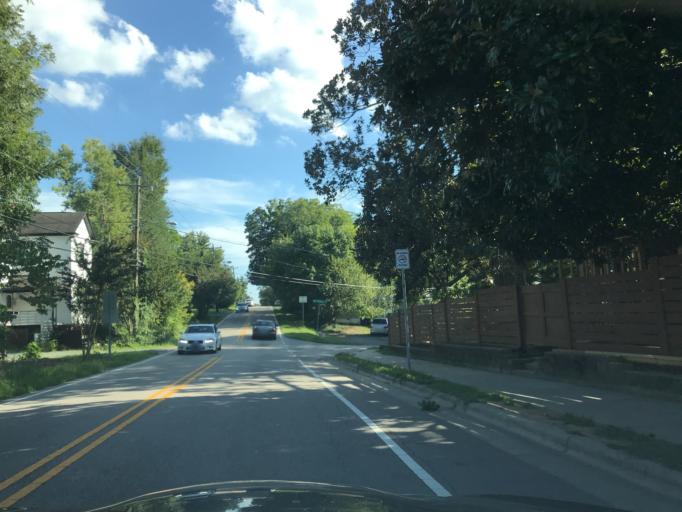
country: US
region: North Carolina
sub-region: Orange County
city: Carrboro
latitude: 35.9091
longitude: -79.0724
